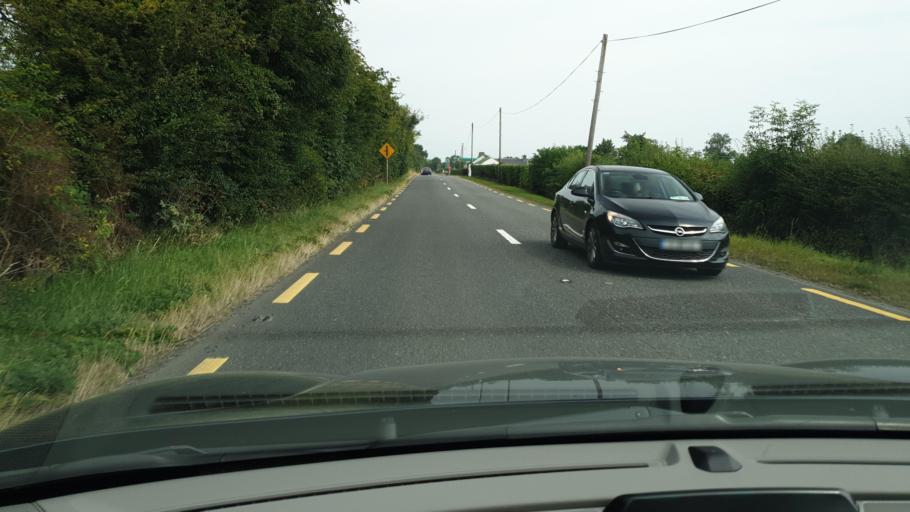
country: IE
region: Leinster
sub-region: An Mhi
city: Athboy
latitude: 53.6772
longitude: -6.9566
